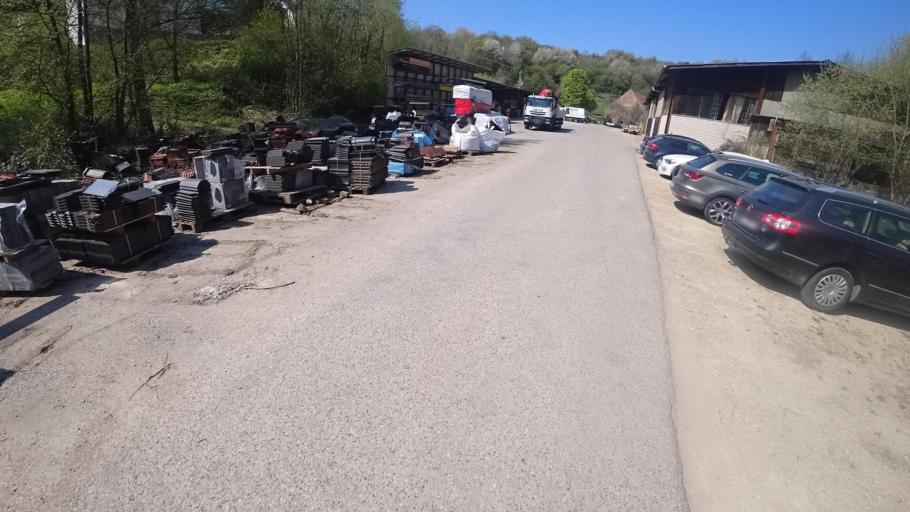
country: DE
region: Rheinland-Pfalz
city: Tawern
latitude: 49.6783
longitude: 6.5079
